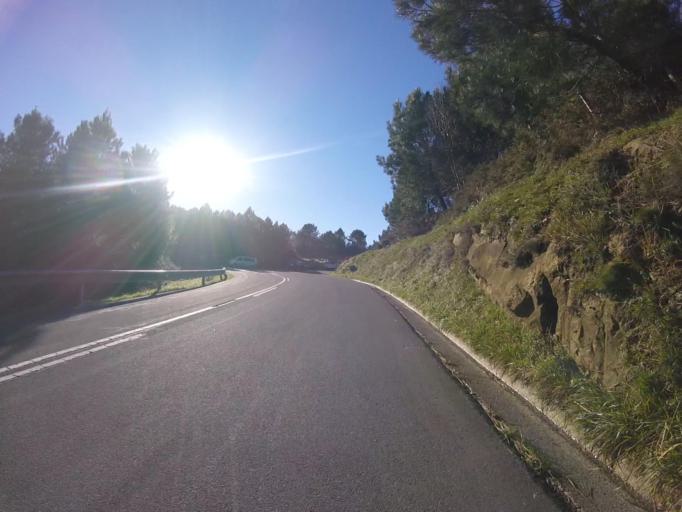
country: ES
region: Basque Country
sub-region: Provincia de Guipuzcoa
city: Lezo
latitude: 43.3355
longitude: -1.8850
